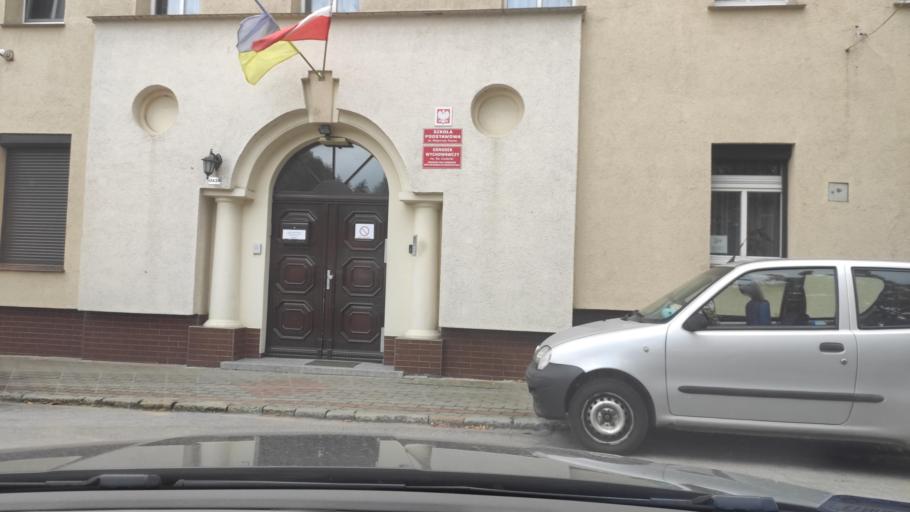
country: PL
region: Greater Poland Voivodeship
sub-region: Powiat poznanski
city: Czerwonak
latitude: 52.4231
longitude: 16.9703
